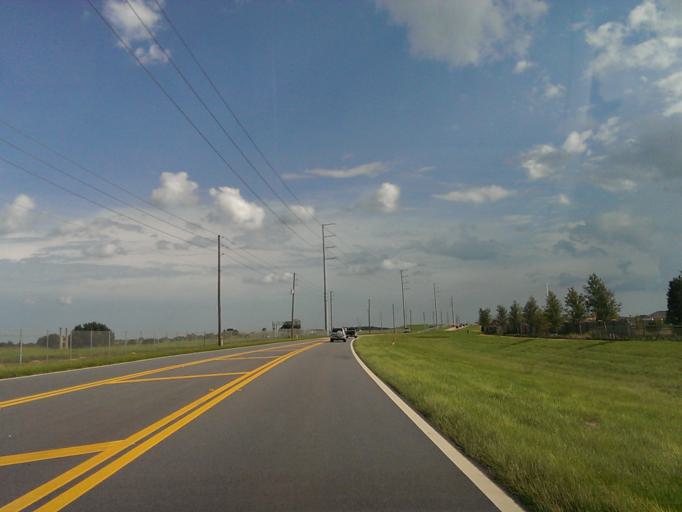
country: US
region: Florida
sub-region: Polk County
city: Citrus Ridge
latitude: 28.4314
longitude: -81.6365
